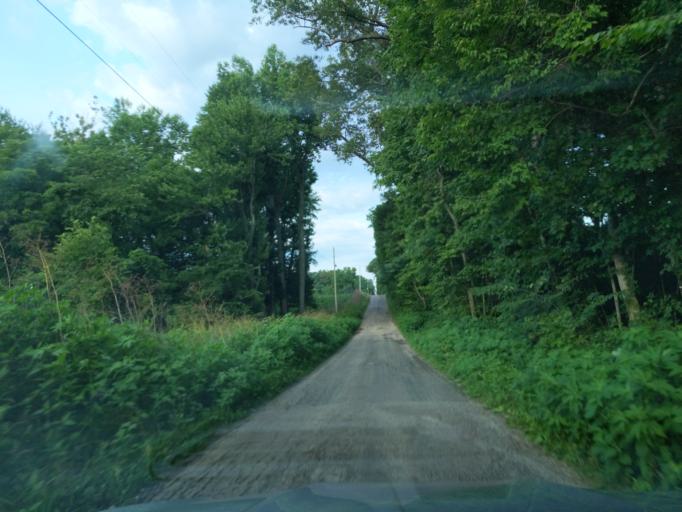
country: US
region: Indiana
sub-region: Ripley County
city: Sunman
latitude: 39.3101
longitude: -85.0891
